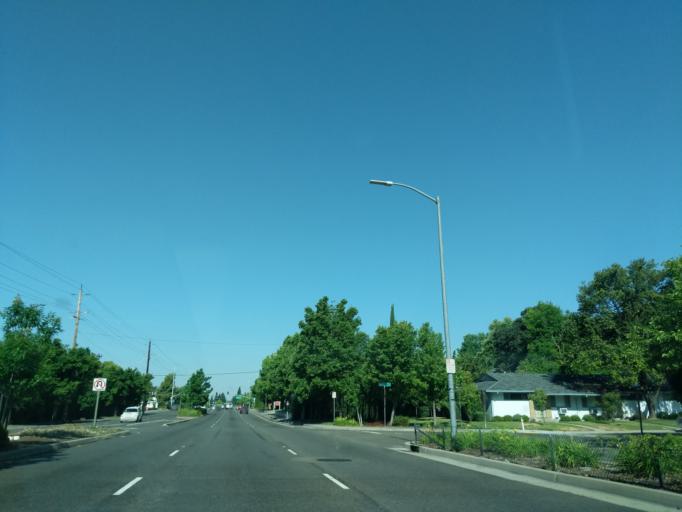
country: US
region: California
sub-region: Sacramento County
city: Antelope
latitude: 38.6782
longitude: -121.3076
